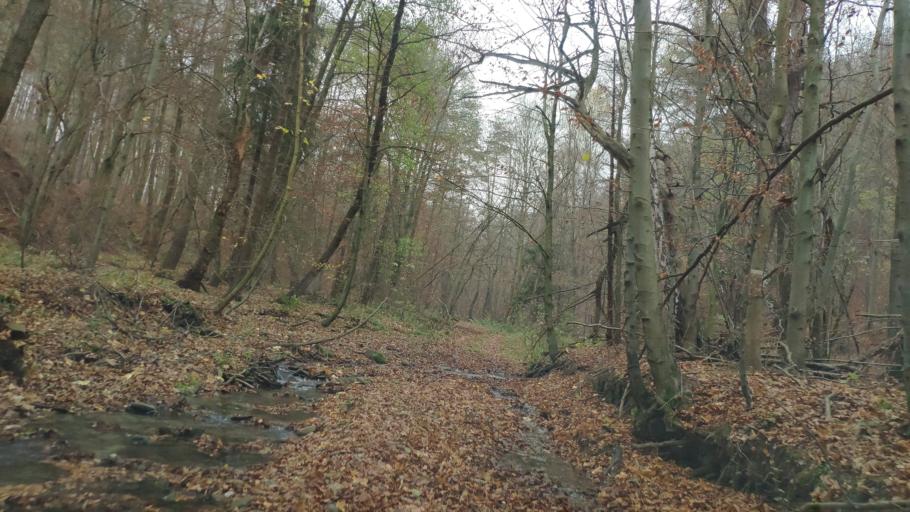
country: SK
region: Presovsky
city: Sabinov
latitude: 49.1482
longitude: 21.2120
